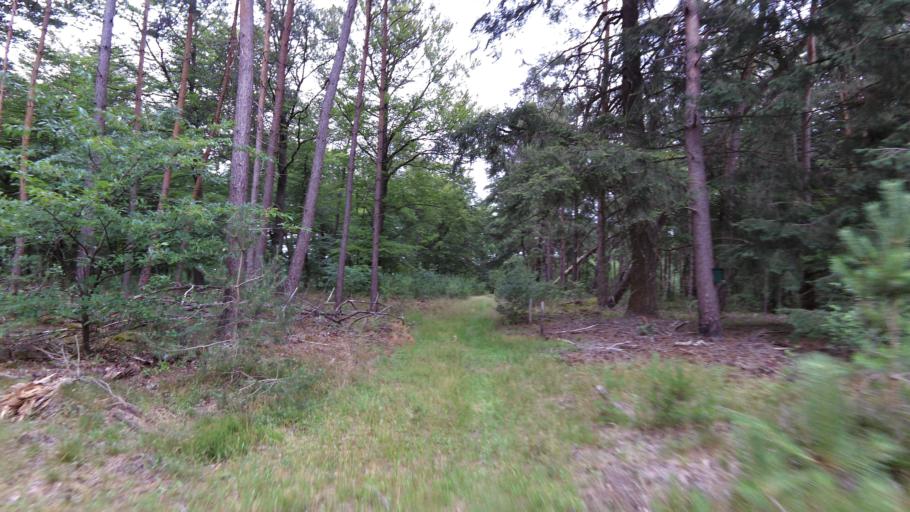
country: NL
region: Gelderland
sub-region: Gemeente Apeldoorn
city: Uddel
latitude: 52.2327
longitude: 5.7855
